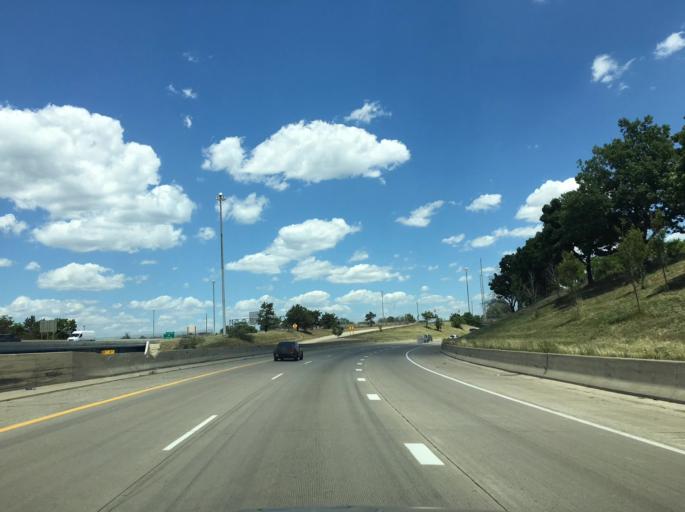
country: US
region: Michigan
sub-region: Wayne County
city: Detroit
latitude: 42.3290
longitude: -83.0859
